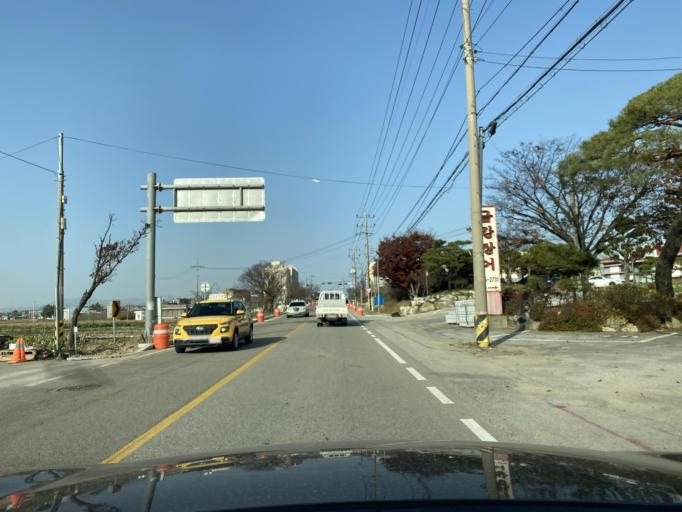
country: KR
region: Chungcheongnam-do
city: Yesan
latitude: 36.6855
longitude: 126.8031
